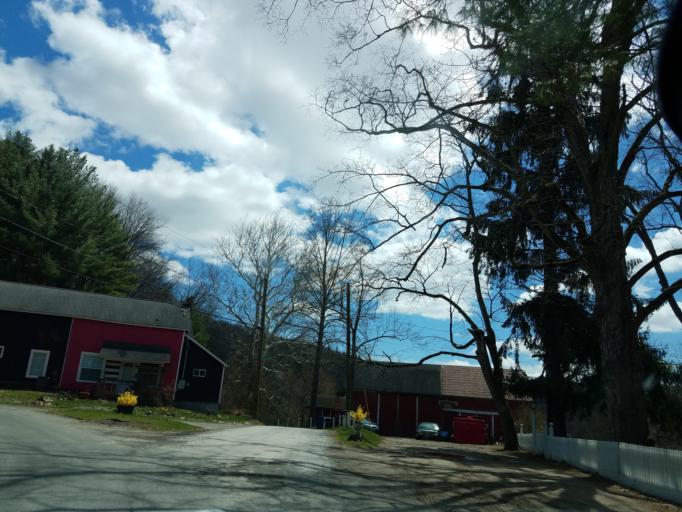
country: US
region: Connecticut
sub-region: Fairfield County
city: Sherman
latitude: 41.6456
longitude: -73.4788
